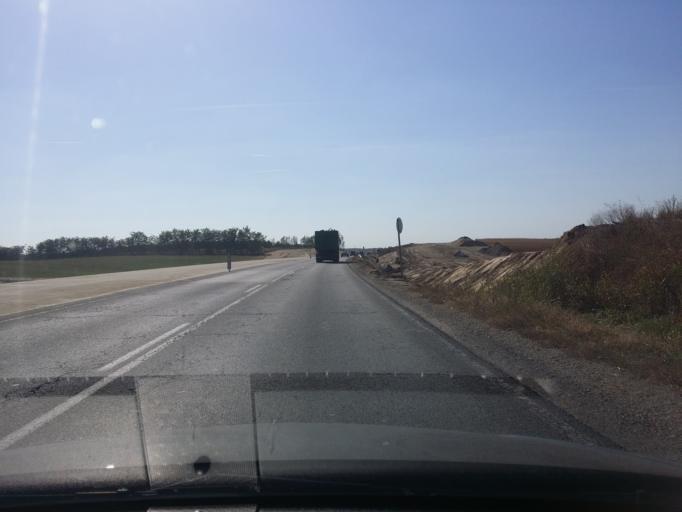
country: HU
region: Bacs-Kiskun
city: Kecskemet
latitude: 46.8631
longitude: 19.6803
